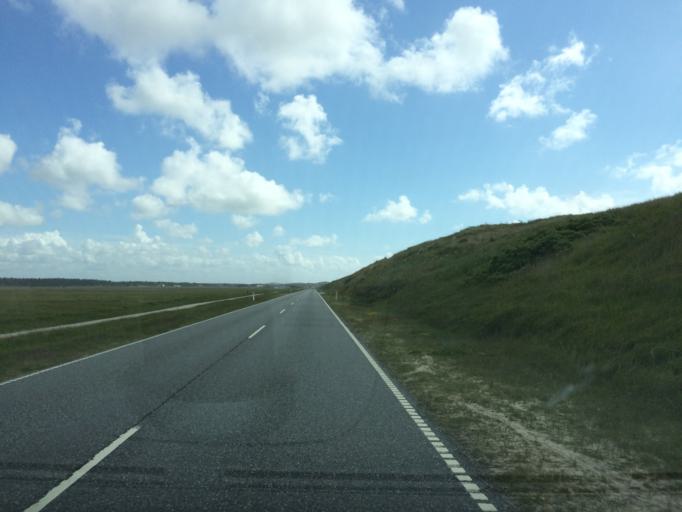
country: DK
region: Central Jutland
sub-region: Holstebro Kommune
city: Ulfborg
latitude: 56.3340
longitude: 8.1228
